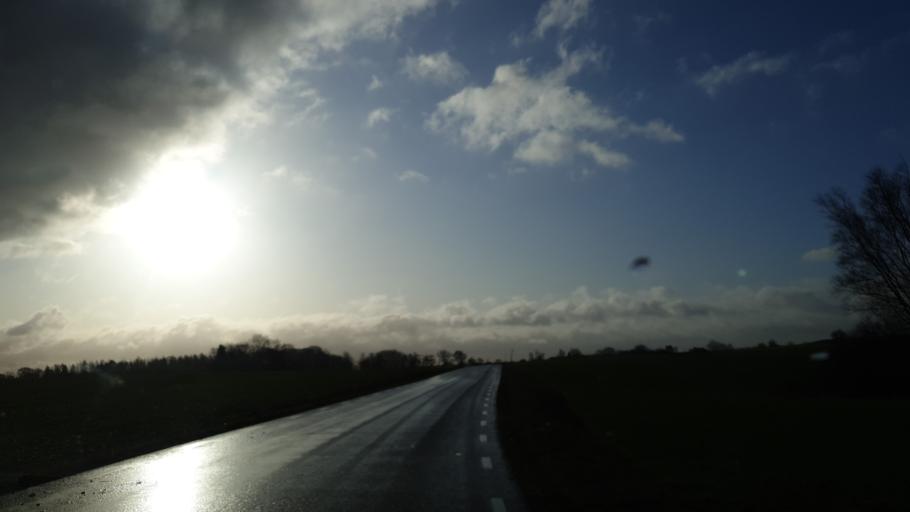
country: SE
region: Skane
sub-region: Skurups Kommun
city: Rydsgard
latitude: 55.4566
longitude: 13.5528
